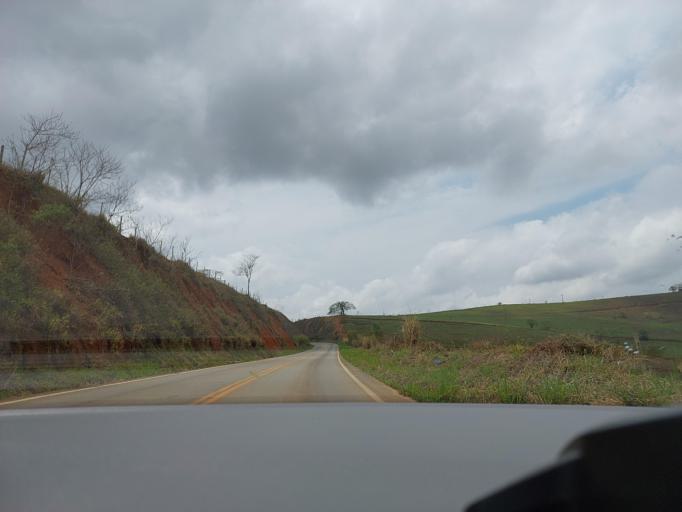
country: BR
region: Minas Gerais
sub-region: Ponte Nova
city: Ponte Nova
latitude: -20.3836
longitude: -42.8771
